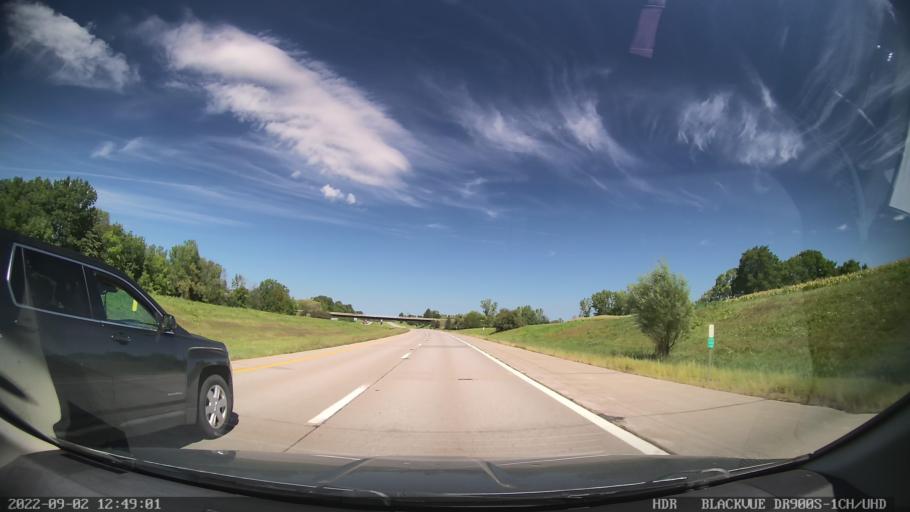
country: US
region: New York
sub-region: Livingston County
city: Livonia
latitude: 42.8428
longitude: -77.7302
